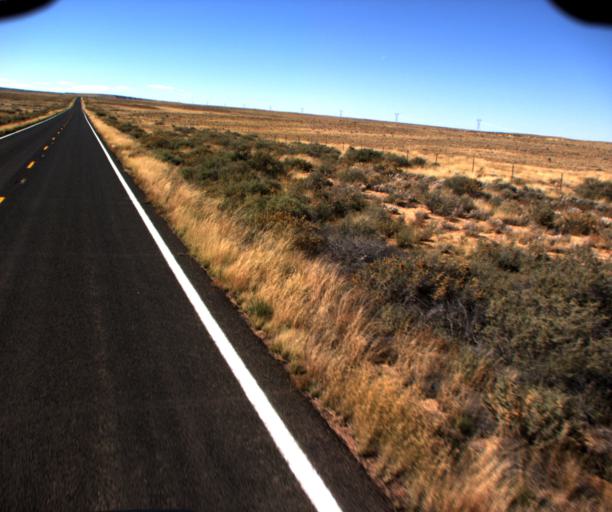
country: US
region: Arizona
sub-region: Navajo County
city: First Mesa
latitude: 35.9720
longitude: -110.7843
